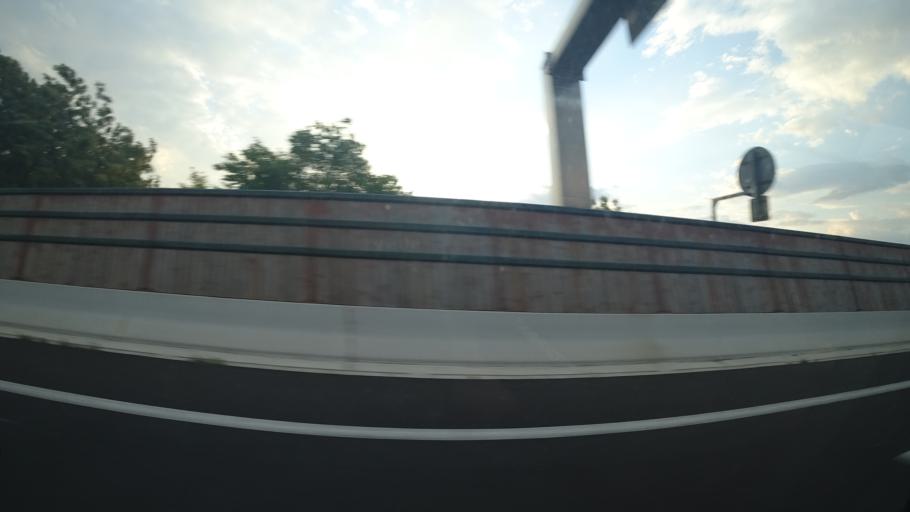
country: FR
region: Languedoc-Roussillon
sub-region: Departement de l'Herault
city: Pezenas
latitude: 43.4558
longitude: 3.4314
